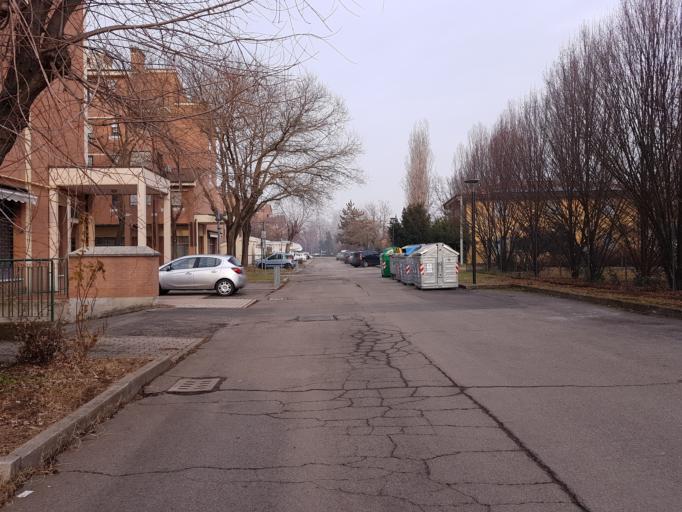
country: IT
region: Emilia-Romagna
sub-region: Provincia di Bologna
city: Quarto Inferiore
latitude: 44.5109
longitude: 11.3855
